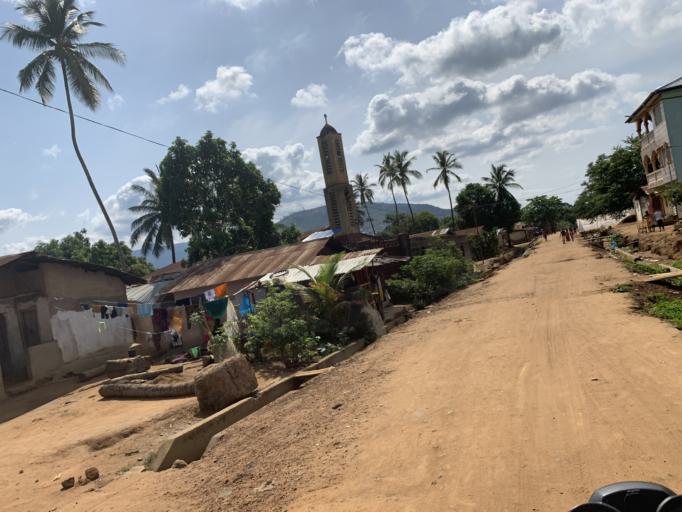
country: SL
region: Western Area
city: Waterloo
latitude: 8.3297
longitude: -13.0628
